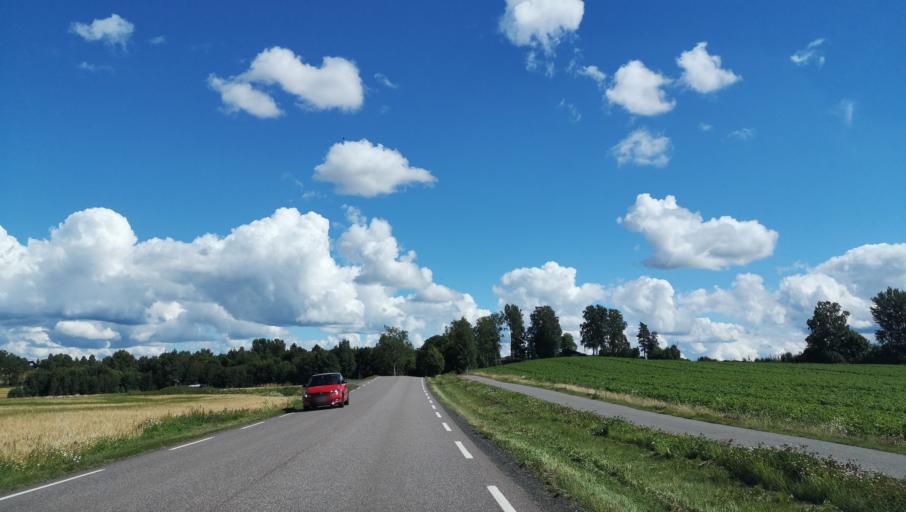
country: NO
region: Akershus
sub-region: Frogn
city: Drobak
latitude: 59.6565
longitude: 10.6970
